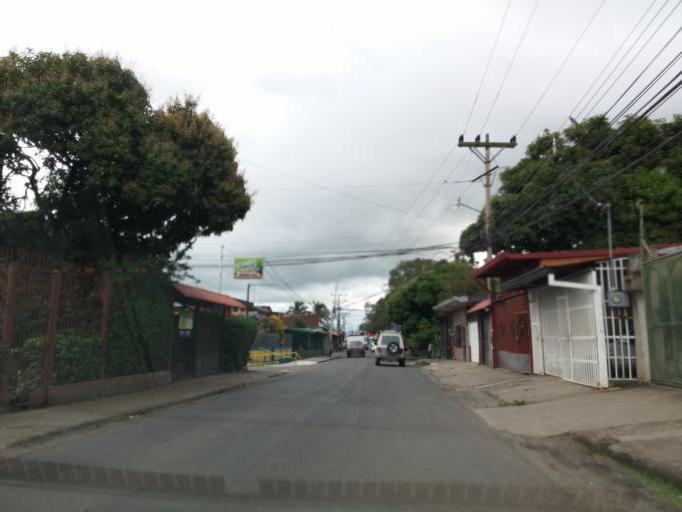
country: CR
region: Alajuela
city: Alajuela
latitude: 10.0028
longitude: -84.2169
